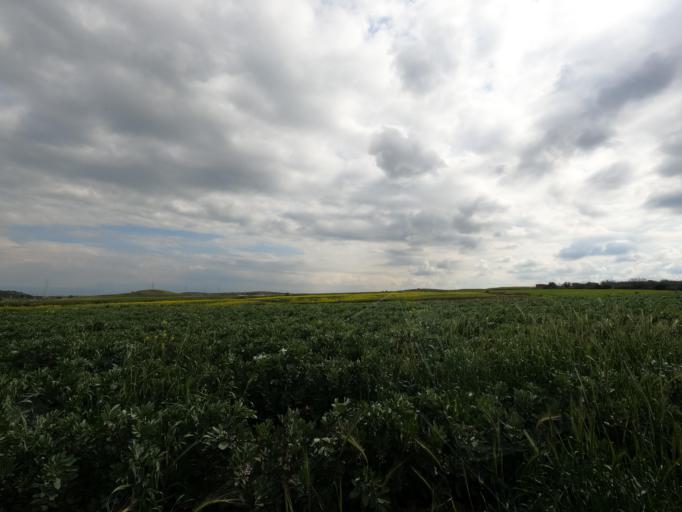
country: CY
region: Lefkosia
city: Astromeritis
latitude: 35.0801
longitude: 32.9581
